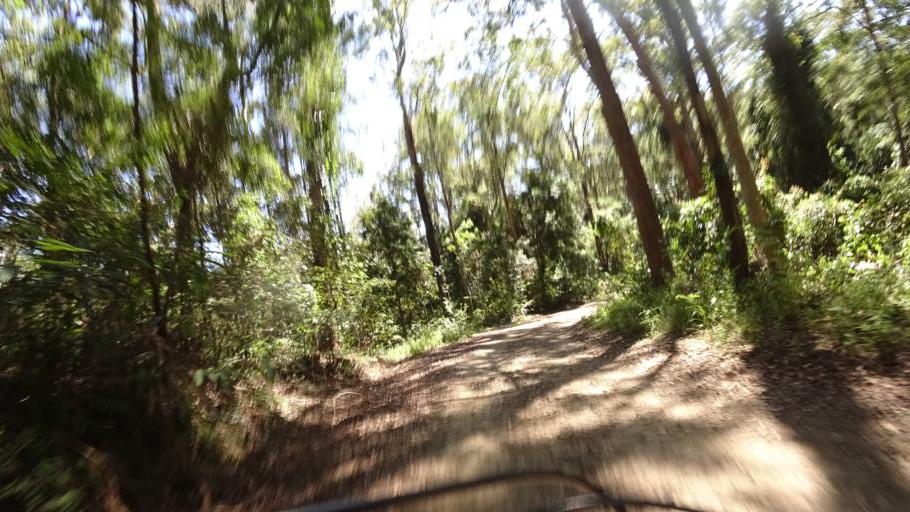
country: AU
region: Queensland
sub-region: Moreton Bay
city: Highvale
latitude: -27.4044
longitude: 152.8000
